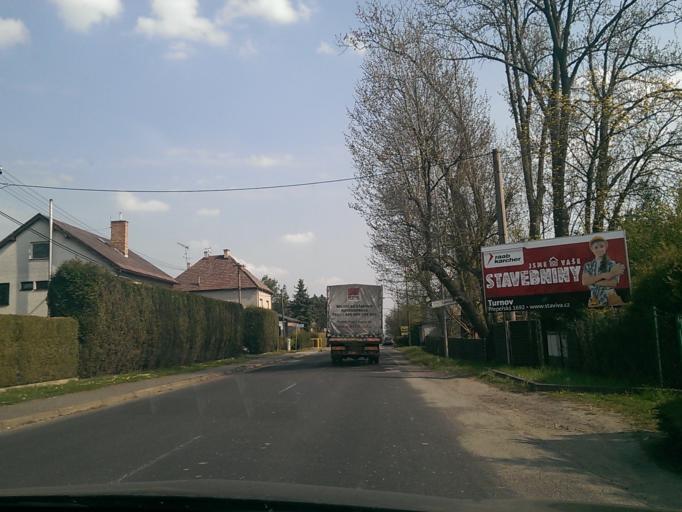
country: CZ
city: Ohrazenice
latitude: 50.5933
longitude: 15.1264
